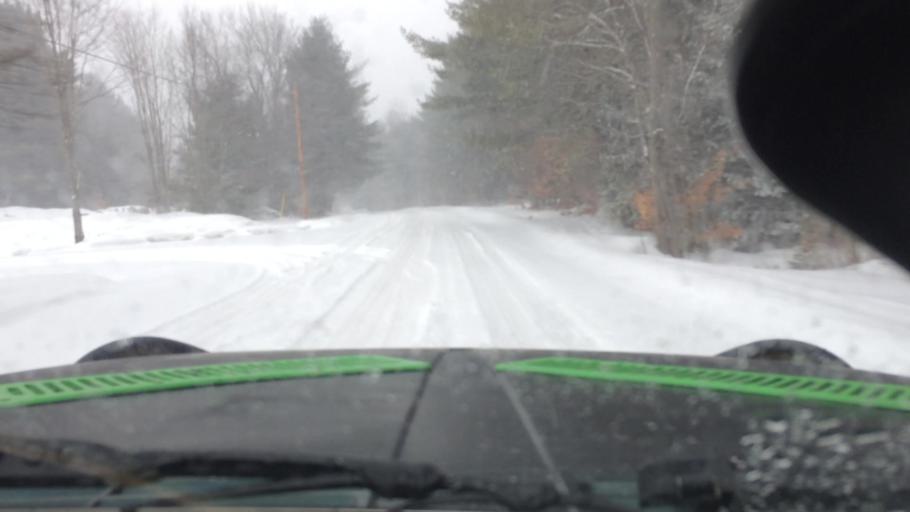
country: US
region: New York
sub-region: Oswego County
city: Constantia
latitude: 43.3062
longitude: -75.9214
